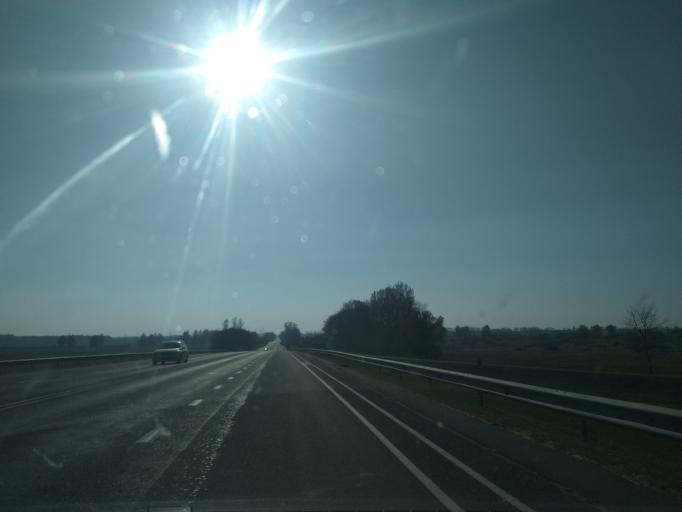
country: BY
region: Brest
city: Kobryn
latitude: 52.1801
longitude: 24.3277
